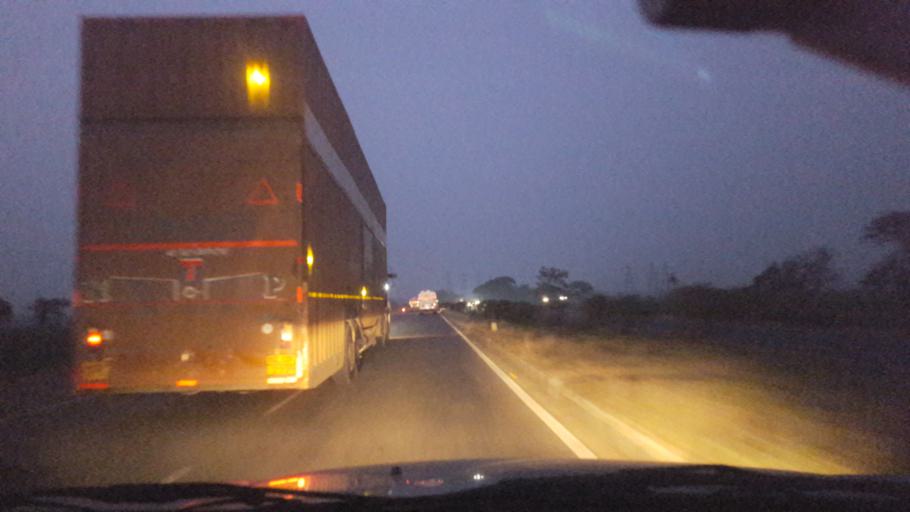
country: IN
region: Andhra Pradesh
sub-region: East Godavari
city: Rajahmundry
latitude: 17.1023
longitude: 81.9179
